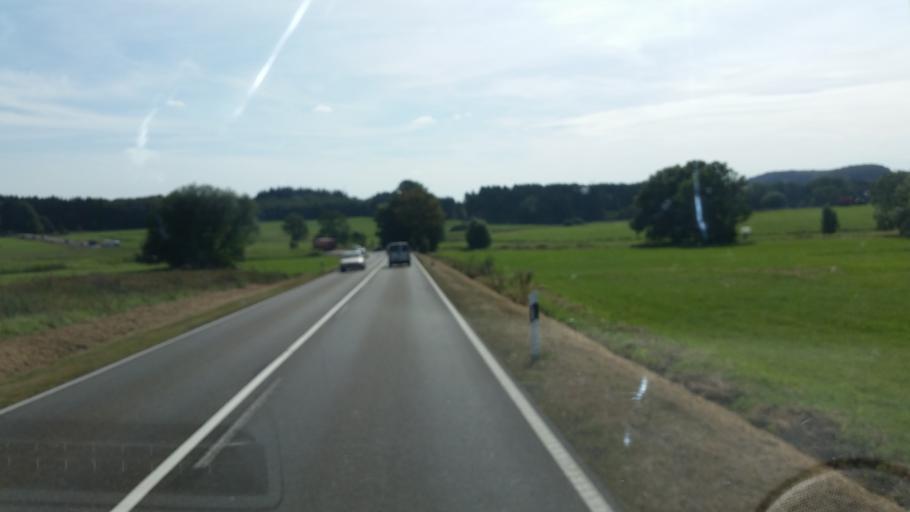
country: DE
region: Rheinland-Pfalz
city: Kaden
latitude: 50.5496
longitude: 7.8846
